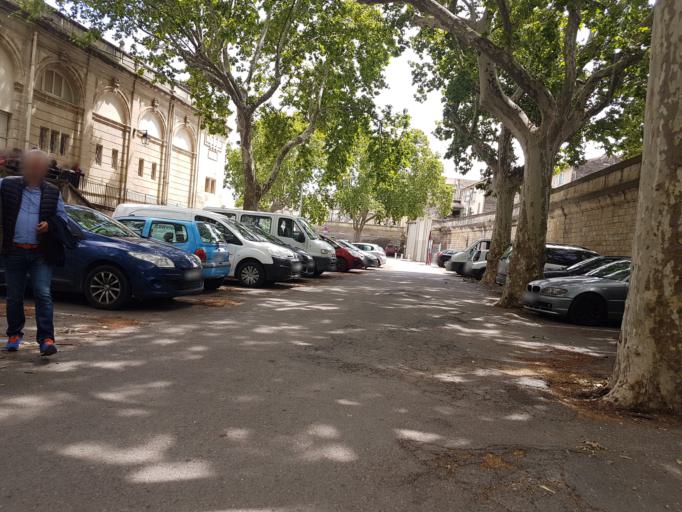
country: FR
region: Languedoc-Roussillon
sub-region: Departement du Gard
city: Beaucaire
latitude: 43.8091
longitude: 4.6469
